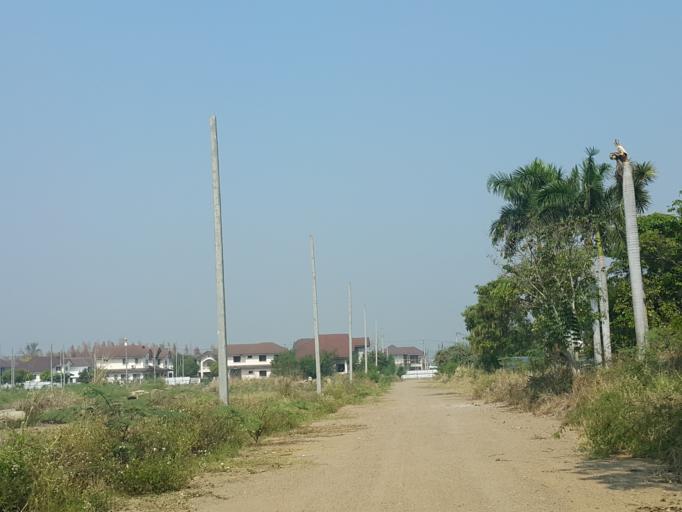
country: TH
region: Chiang Mai
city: Hang Dong
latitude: 18.7146
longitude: 98.9646
